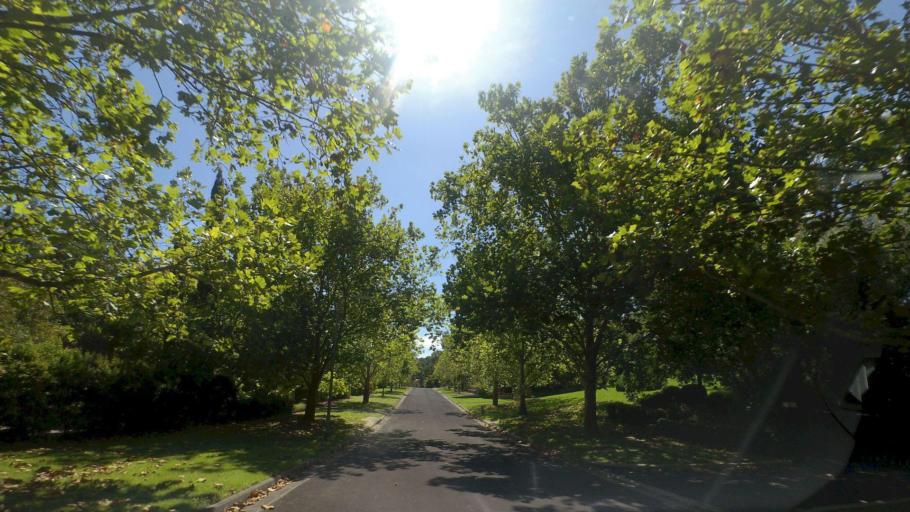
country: AU
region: Victoria
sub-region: Nillumbik
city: North Warrandyte
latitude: -37.7475
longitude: 145.1940
